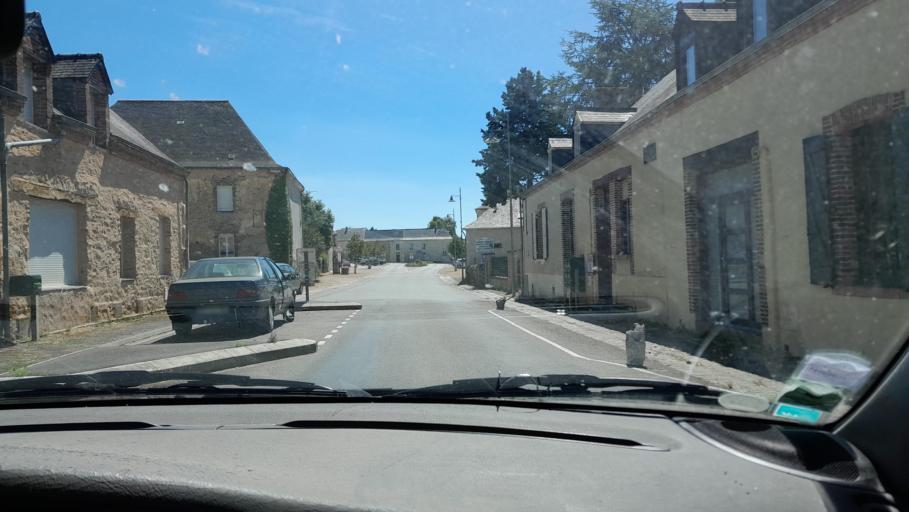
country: FR
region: Pays de la Loire
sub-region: Departement de la Mayenne
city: Ballots
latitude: 47.8973
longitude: -1.1107
